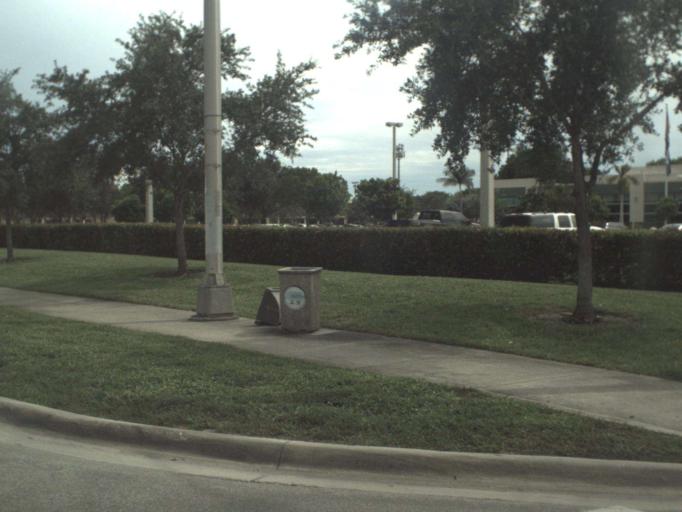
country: US
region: Florida
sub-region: Miami-Dade County
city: Country Club
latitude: 25.9398
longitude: -80.2984
